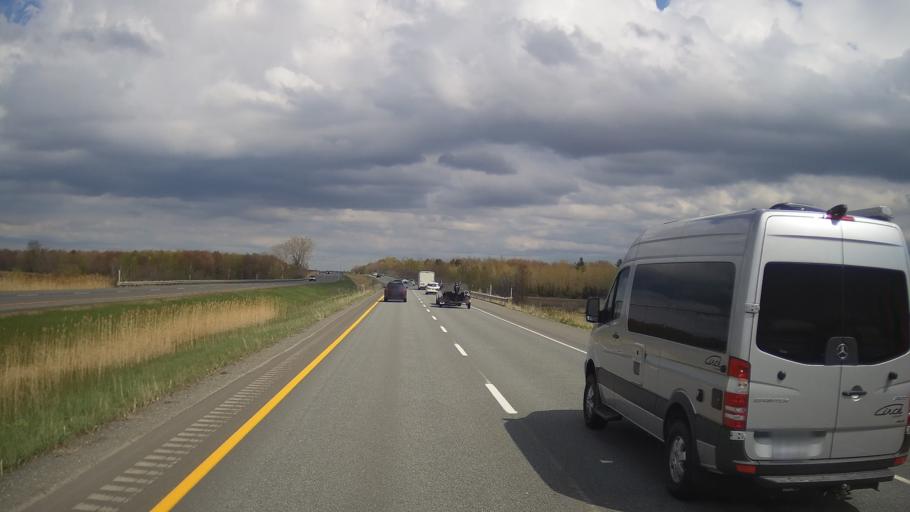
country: CA
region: Quebec
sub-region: Monteregie
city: Granby
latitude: 45.3496
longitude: -72.8458
